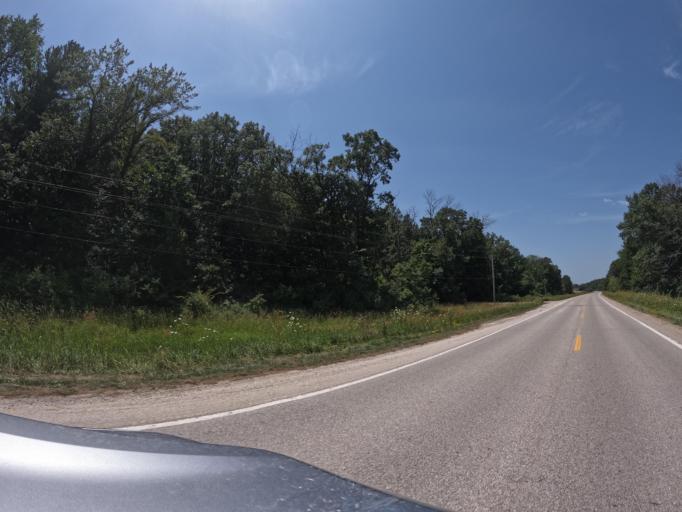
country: US
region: Iowa
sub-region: Henry County
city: Mount Pleasant
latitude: 40.9381
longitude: -91.5866
